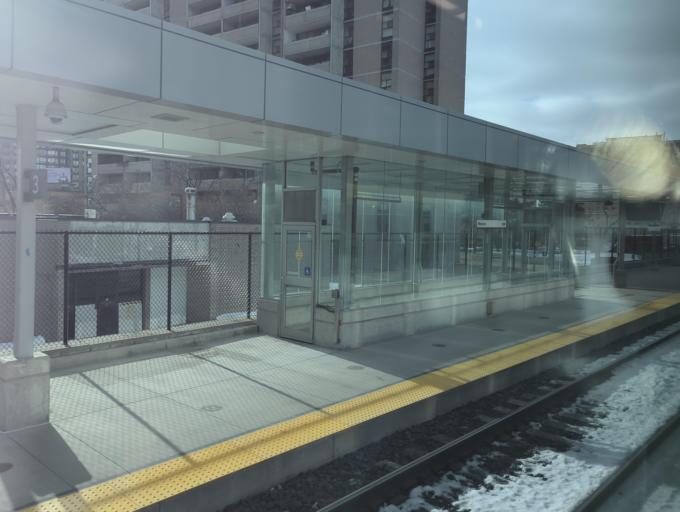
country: CA
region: Ontario
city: Etobicoke
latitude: 43.6995
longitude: -79.5120
